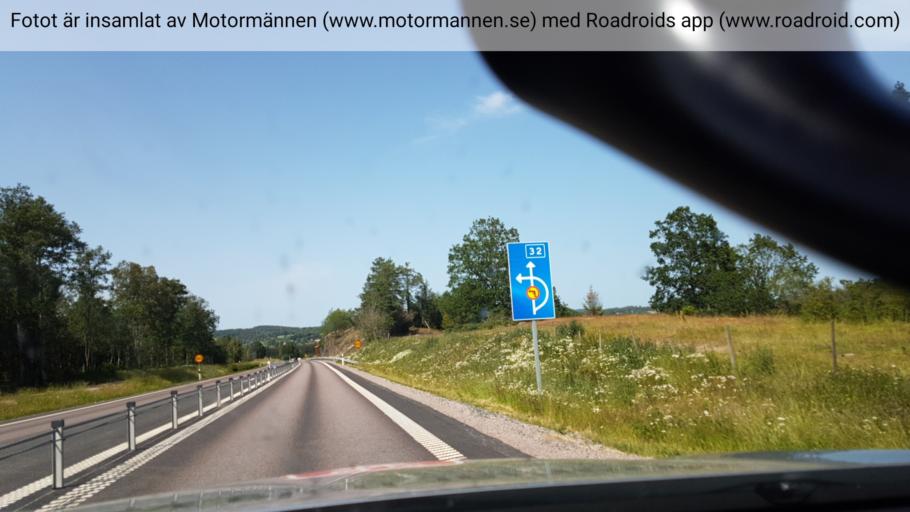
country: SE
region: Joenkoeping
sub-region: Tranas Kommun
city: Tranas
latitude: 57.9722
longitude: 14.9144
